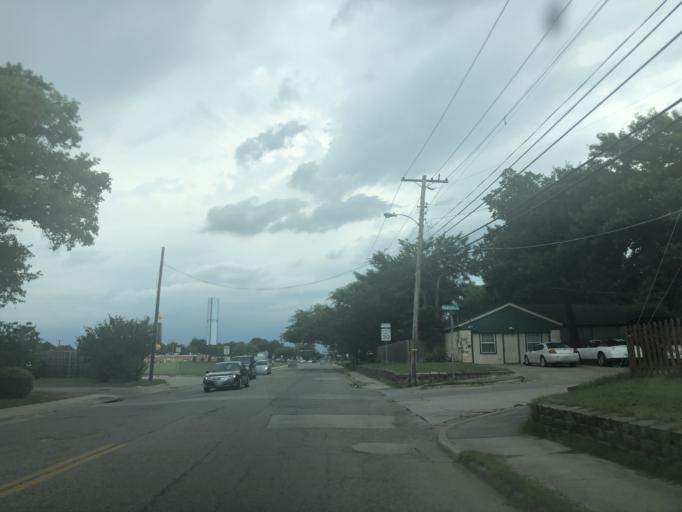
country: US
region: Texas
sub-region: Dallas County
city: Irving
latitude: 32.8057
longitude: -96.9345
